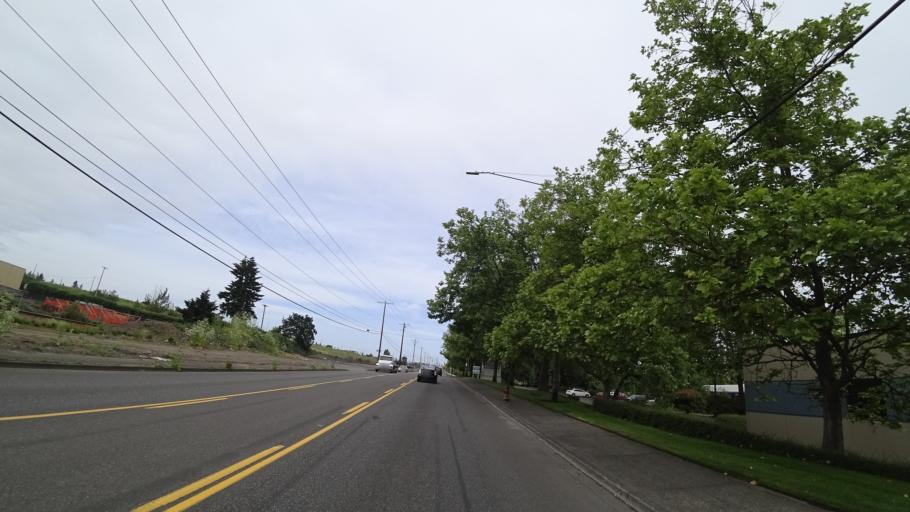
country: US
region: Oregon
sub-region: Multnomah County
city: Lents
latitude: 45.5655
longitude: -122.5823
